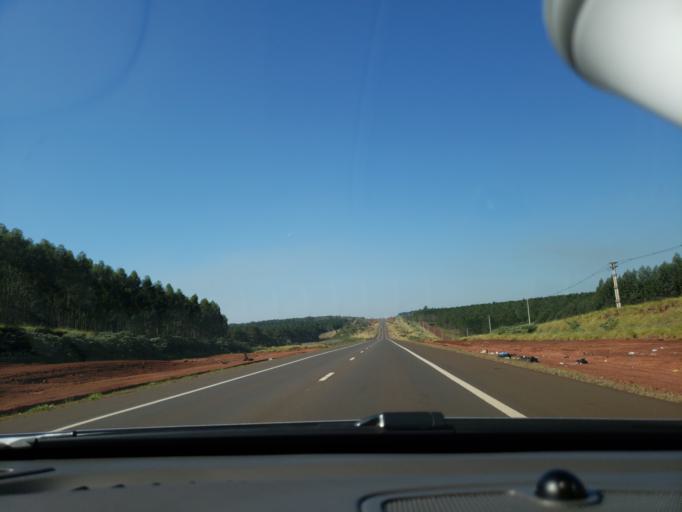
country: AR
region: Misiones
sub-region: Departamento de Capital
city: Posadas
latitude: -27.4654
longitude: -55.9376
